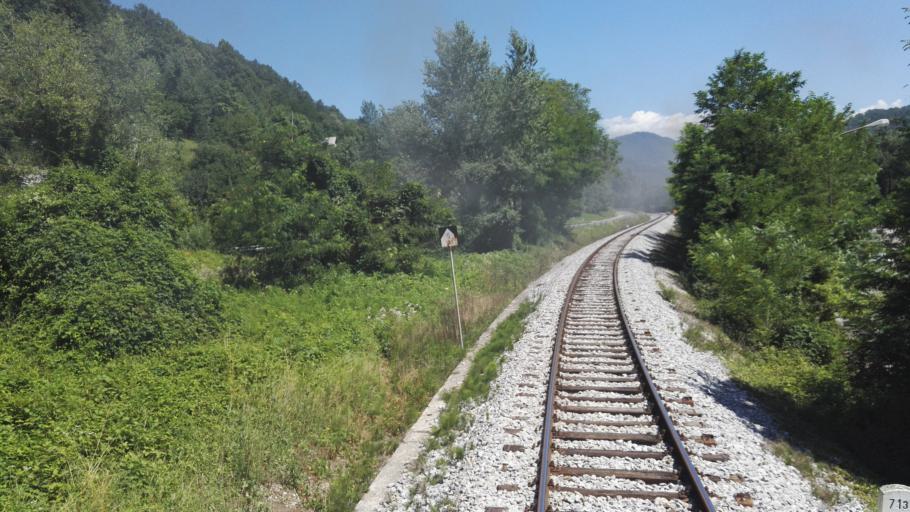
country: SI
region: Kanal
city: Kanal
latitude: 46.0722
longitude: 13.6272
